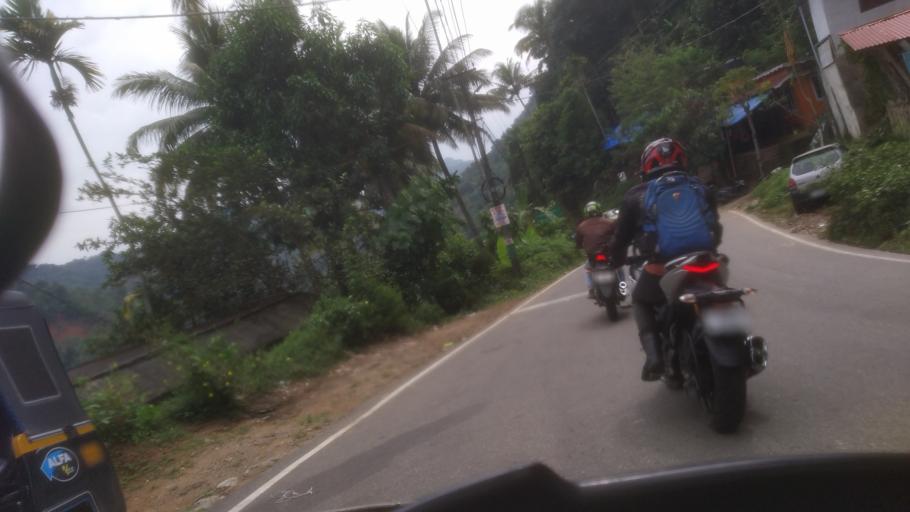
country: IN
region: Kerala
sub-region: Idukki
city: Munnar
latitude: 9.9820
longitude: 76.9995
